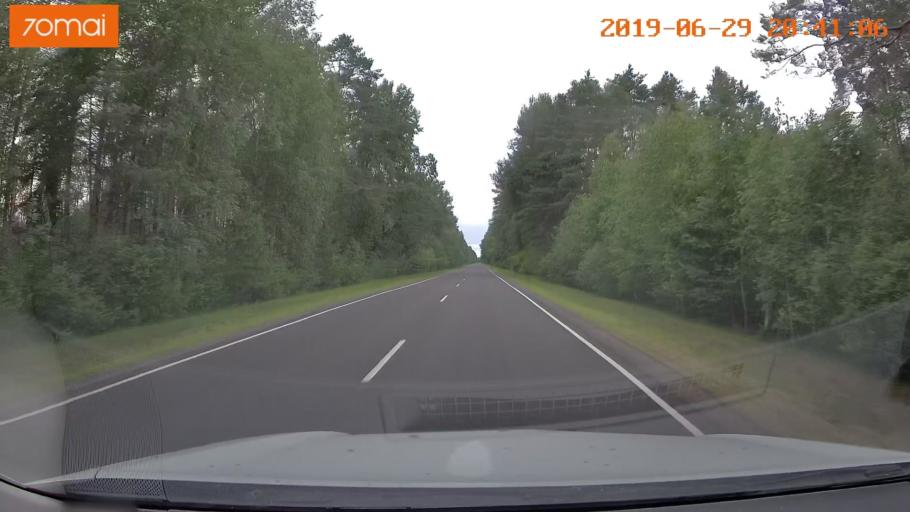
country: BY
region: Brest
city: Hantsavichy
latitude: 52.5817
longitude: 26.3438
